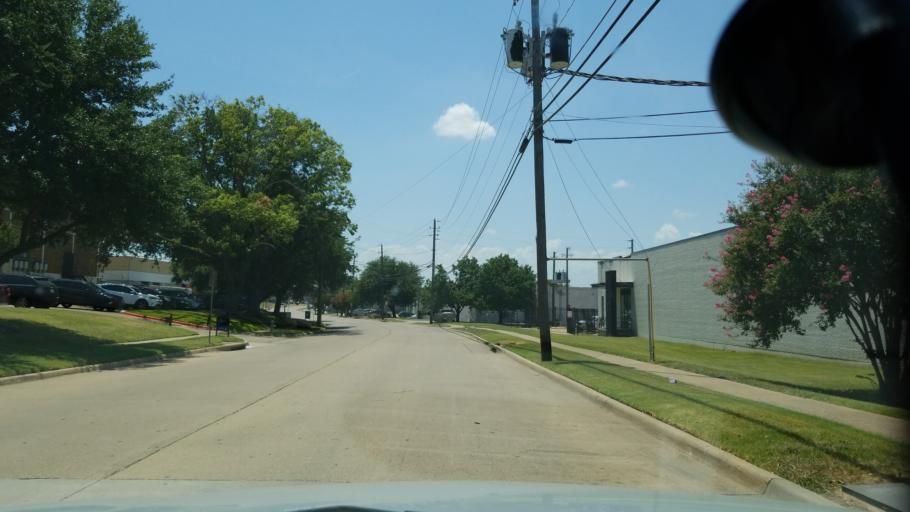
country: US
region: Texas
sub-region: Dallas County
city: Farmers Branch
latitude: 32.8939
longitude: -96.8846
